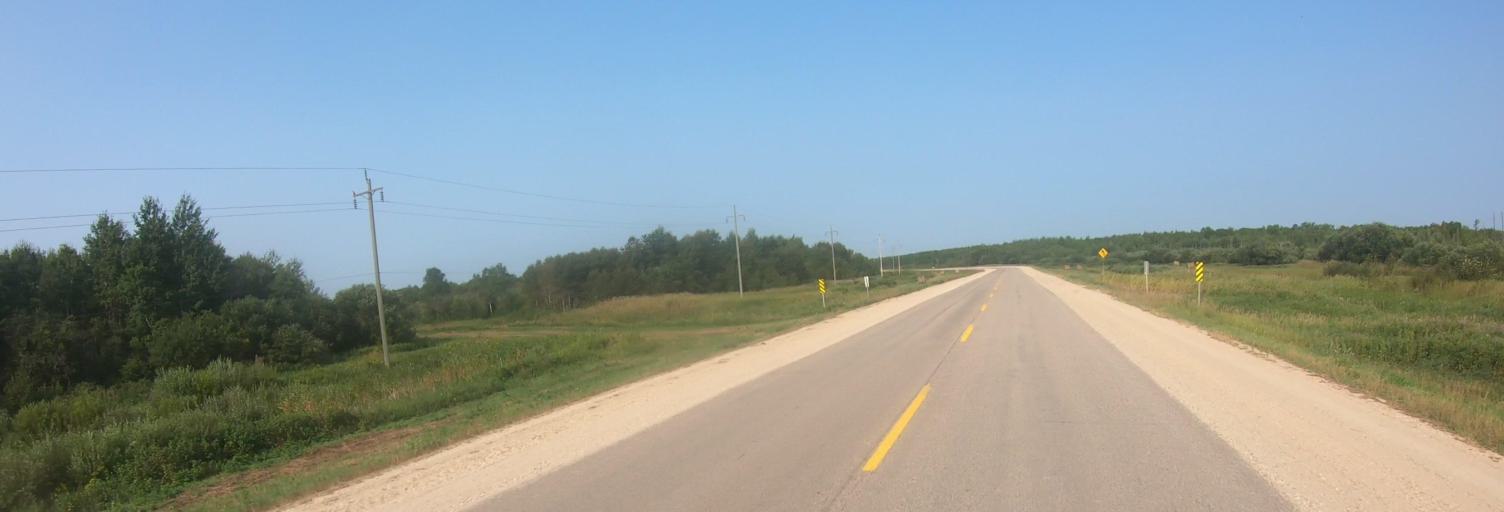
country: US
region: Minnesota
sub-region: Roseau County
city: Roseau
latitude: 49.0221
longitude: -95.5604
